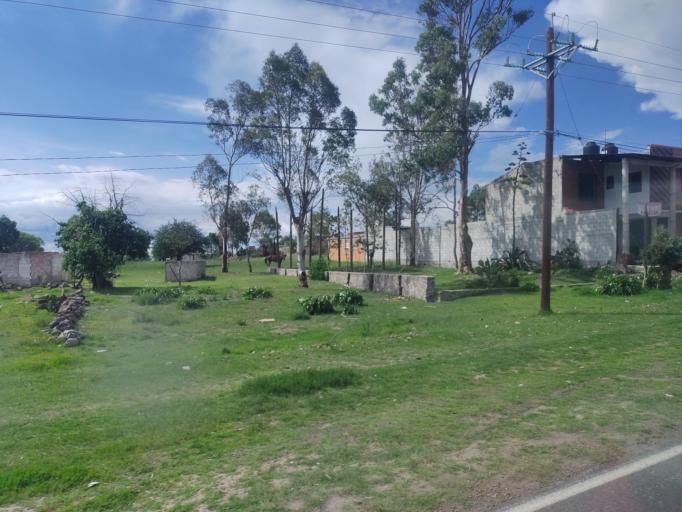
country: MX
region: Mexico
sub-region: Aculco
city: El Colorado
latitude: 20.0946
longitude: -99.7672
